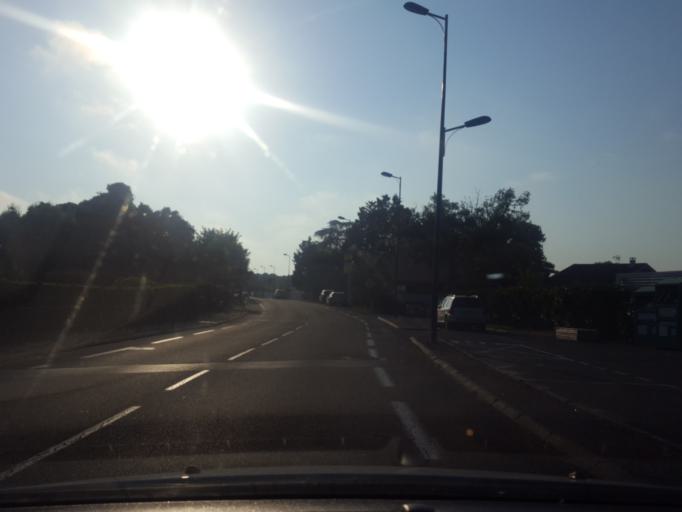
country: FR
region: Aquitaine
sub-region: Departement des Landes
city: Ondres
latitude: 43.5677
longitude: -1.4527
